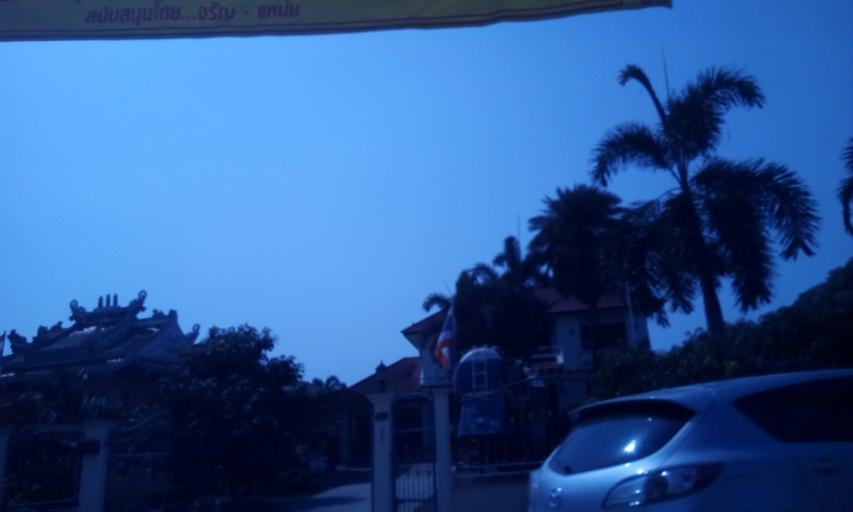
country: TH
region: Nonthaburi
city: Sai Noi
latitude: 13.9812
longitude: 100.3127
